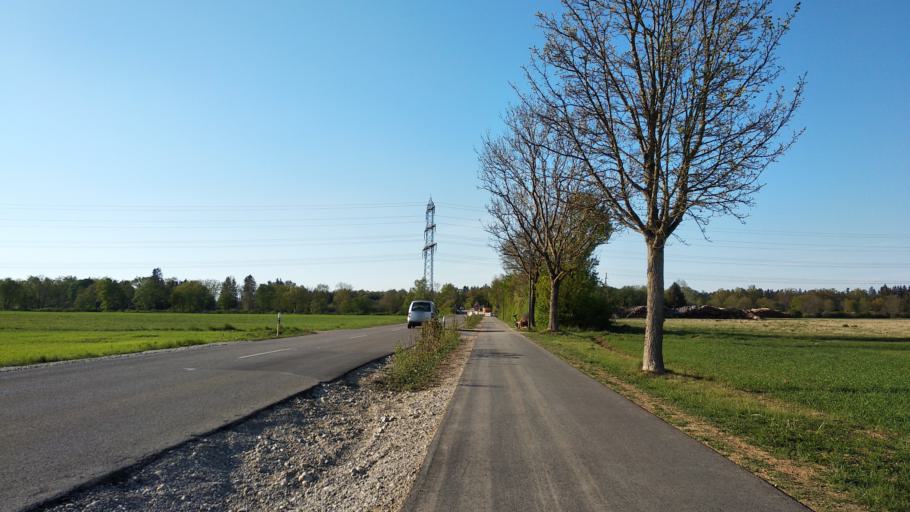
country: DE
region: Bavaria
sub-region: Upper Bavaria
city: Hohenbrunn
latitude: 48.0552
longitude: 11.6999
